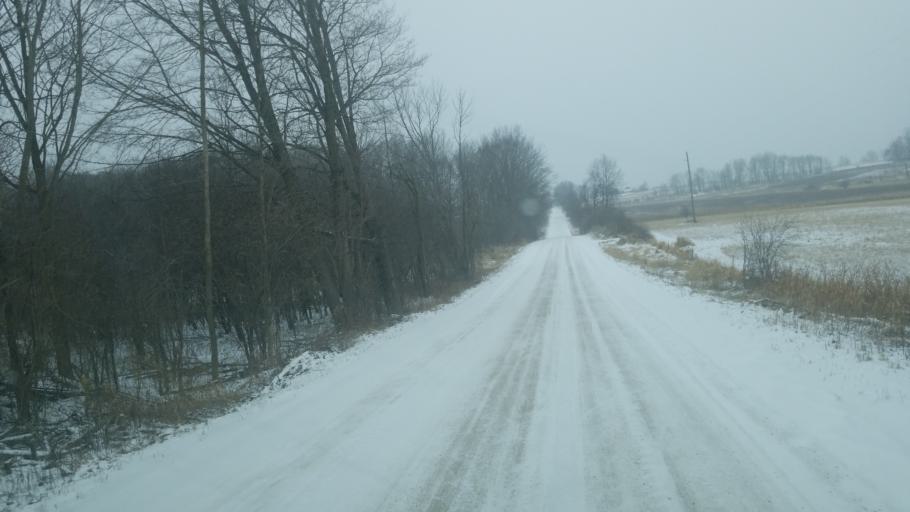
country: US
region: Michigan
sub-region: Osceola County
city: Reed City
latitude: 43.8378
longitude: -85.3939
